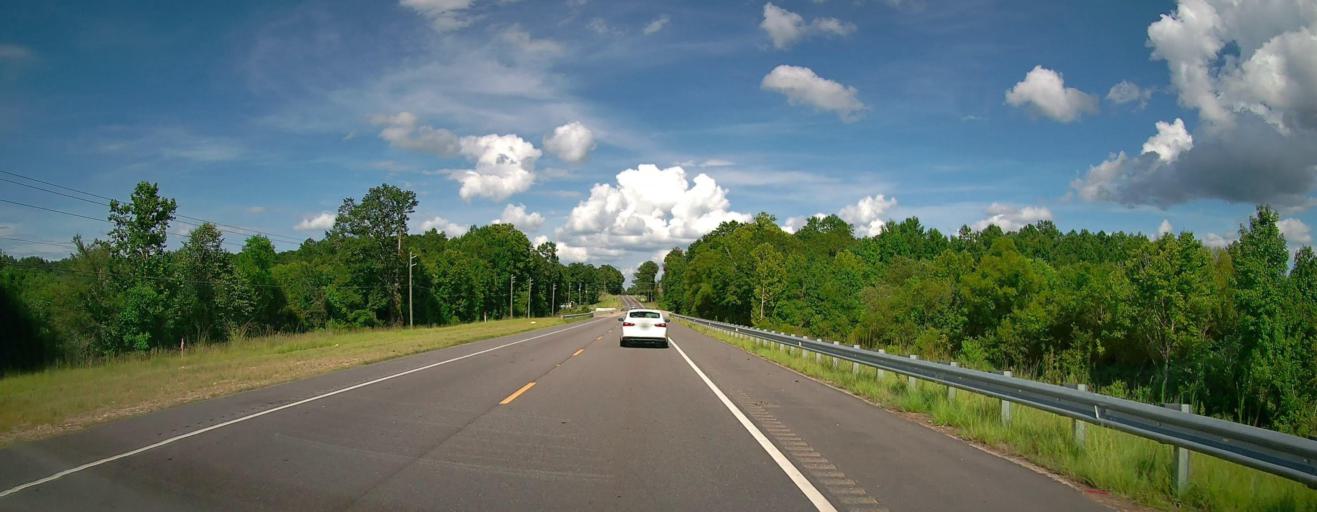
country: US
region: Alabama
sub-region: Russell County
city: Ladonia
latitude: 32.4613
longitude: -85.1345
